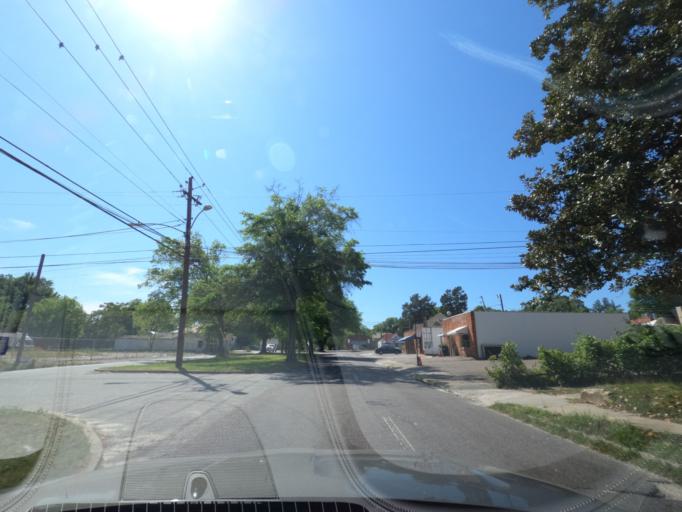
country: US
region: Georgia
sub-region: Richmond County
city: Augusta
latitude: 33.4710
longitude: -82.0269
